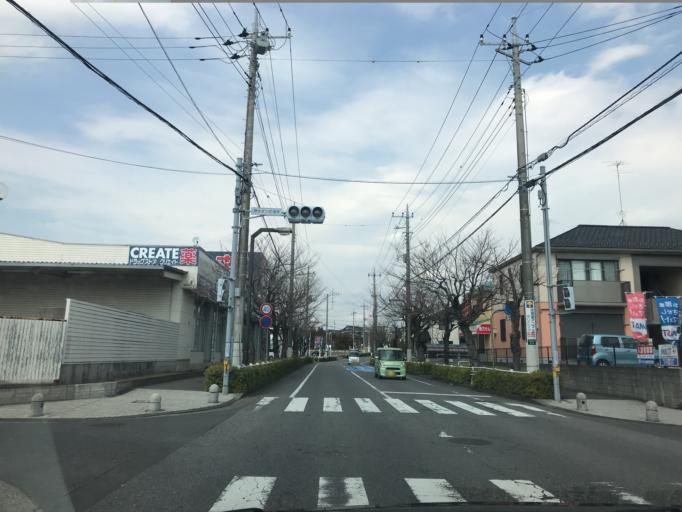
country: JP
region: Ibaraki
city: Mitsukaido
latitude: 35.9783
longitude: 139.9803
